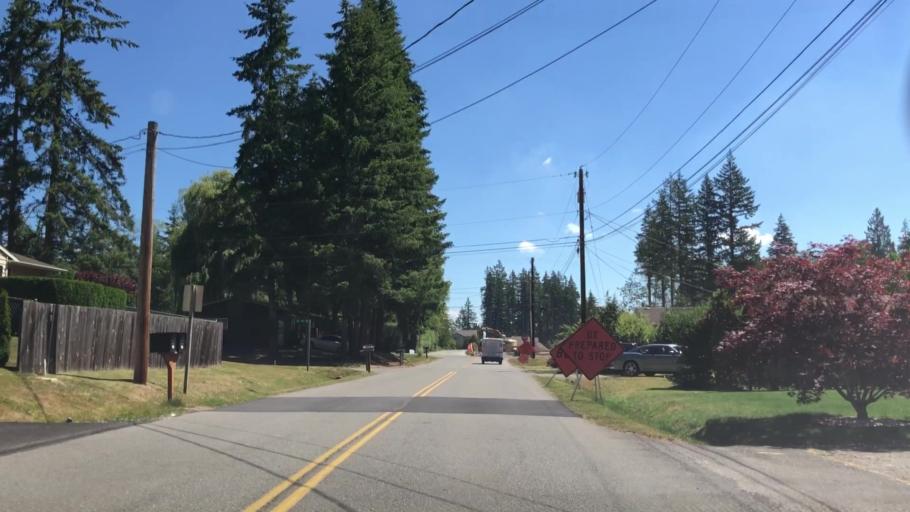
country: US
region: Washington
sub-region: Snohomish County
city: Martha Lake
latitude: 47.8597
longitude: -122.2374
